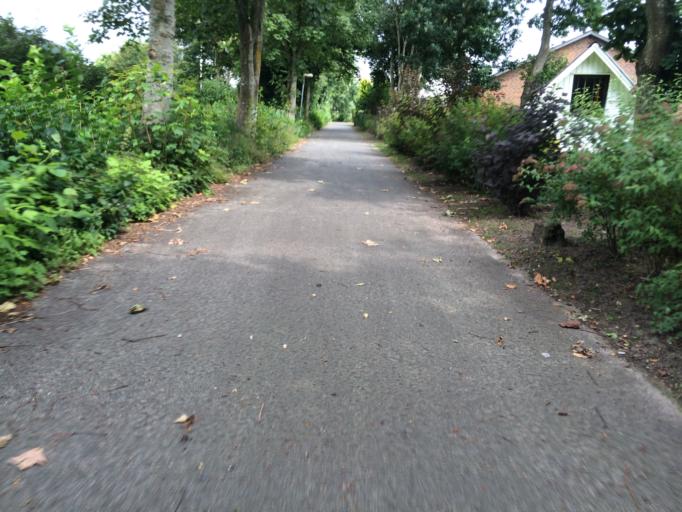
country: DK
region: Central Jutland
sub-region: Holstebro Kommune
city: Ulfborg
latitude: 56.2724
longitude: 8.3088
